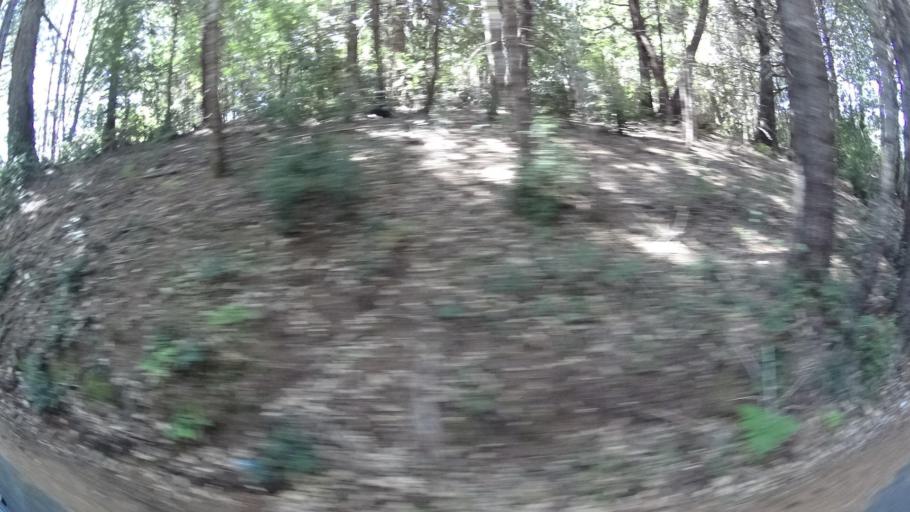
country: US
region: California
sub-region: Humboldt County
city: Redway
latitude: 40.1525
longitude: -124.0379
